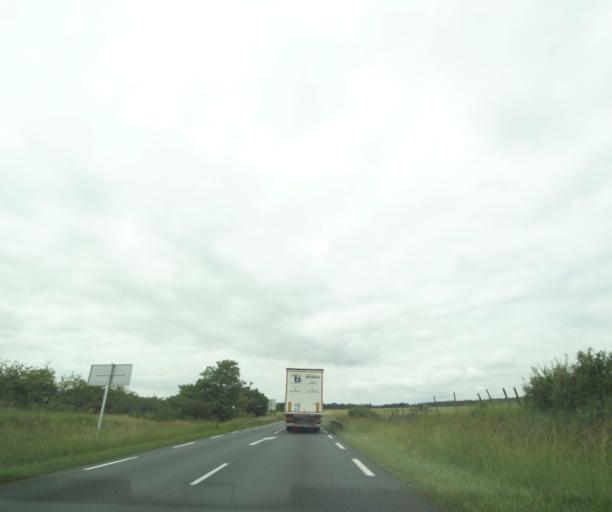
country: FR
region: Pays de la Loire
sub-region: Departement de Maine-et-Loire
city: Montreuil-Bellay
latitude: 47.1375
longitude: -0.1629
